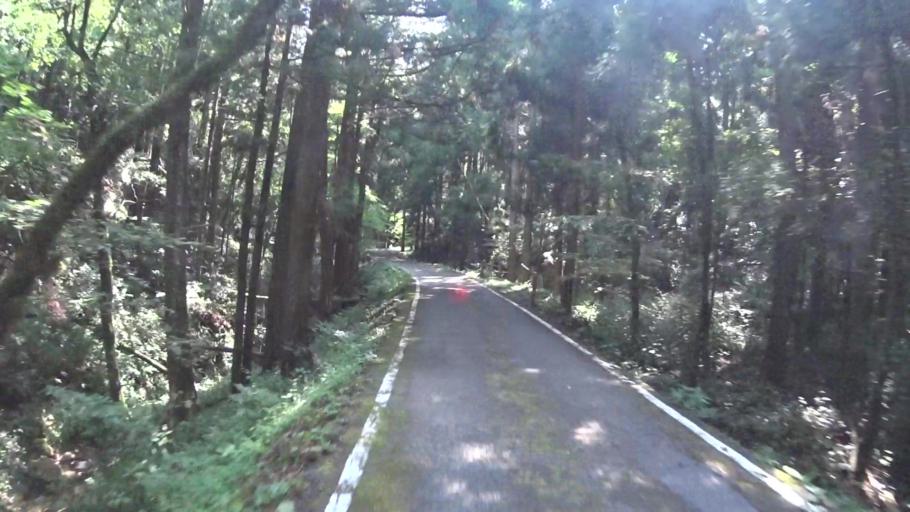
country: JP
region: Kyoto
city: Miyazu
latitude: 35.6592
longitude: 135.1226
